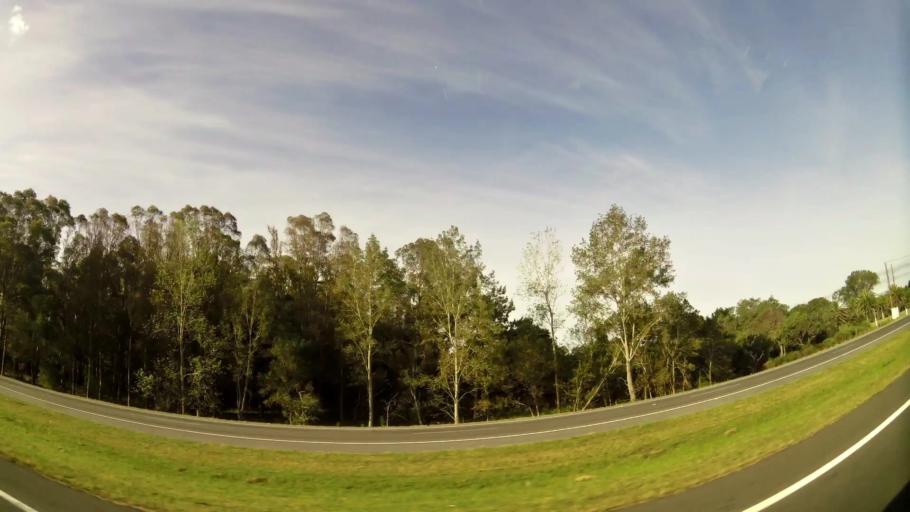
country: UY
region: Canelones
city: La Floresta
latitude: -34.7868
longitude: -55.5225
